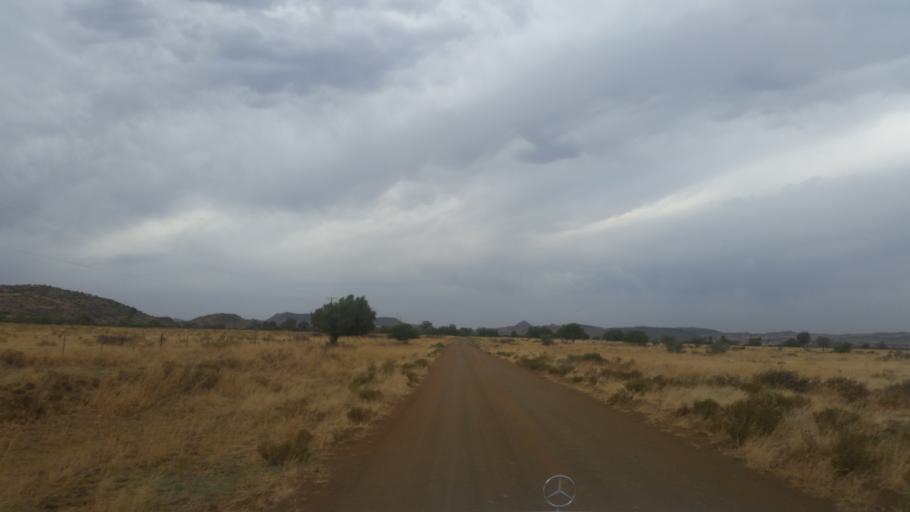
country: ZA
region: Orange Free State
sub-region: Xhariep District Municipality
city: Trompsburg
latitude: -30.5021
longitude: 25.9524
